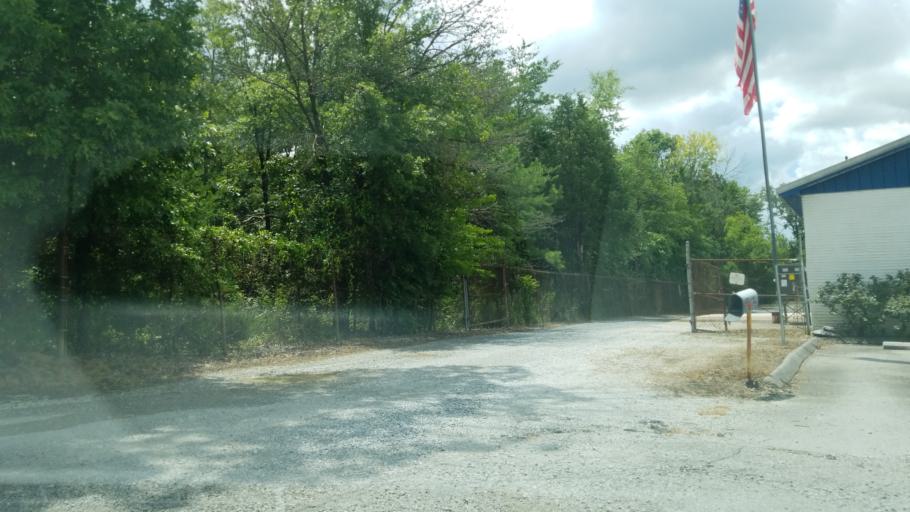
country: US
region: Tennessee
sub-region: Hamilton County
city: East Chattanooga
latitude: 35.0739
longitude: -85.2564
